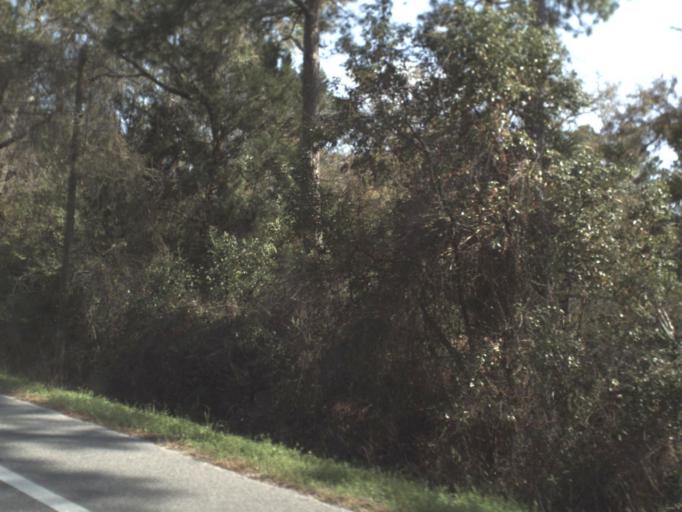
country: US
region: Florida
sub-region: Wakulla County
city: Crawfordville
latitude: 30.0598
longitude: -84.4822
